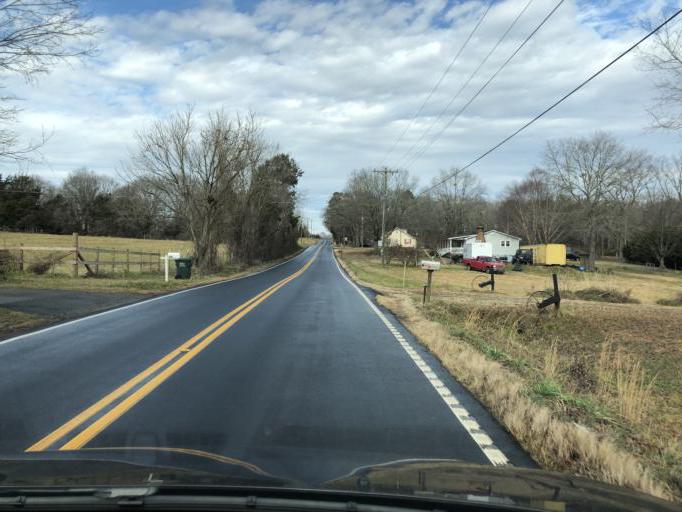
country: US
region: South Carolina
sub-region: Greenville County
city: Five Forks
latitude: 34.8535
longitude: -82.1940
